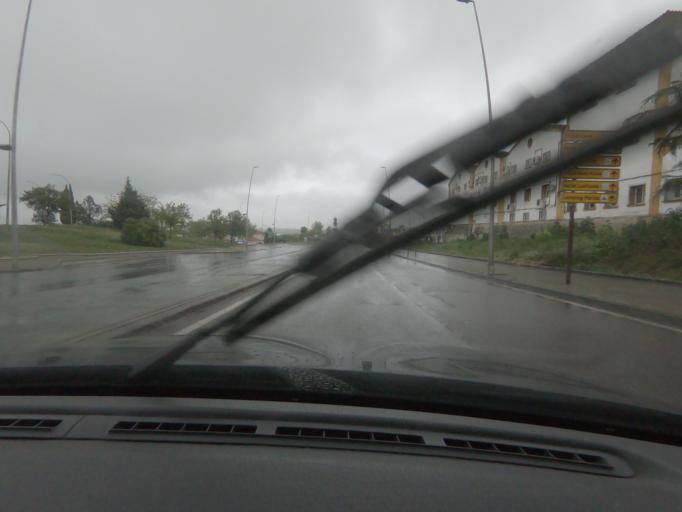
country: ES
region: Extremadura
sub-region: Provincia de Badajoz
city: Merida
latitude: 38.9051
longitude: -6.3654
